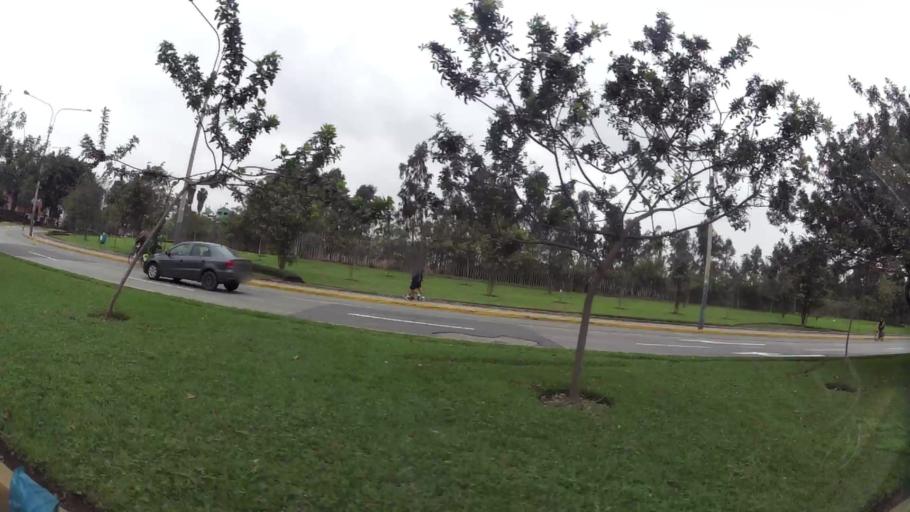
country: PE
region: Lima
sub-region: Lima
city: San Luis
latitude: -12.1079
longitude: -76.9877
